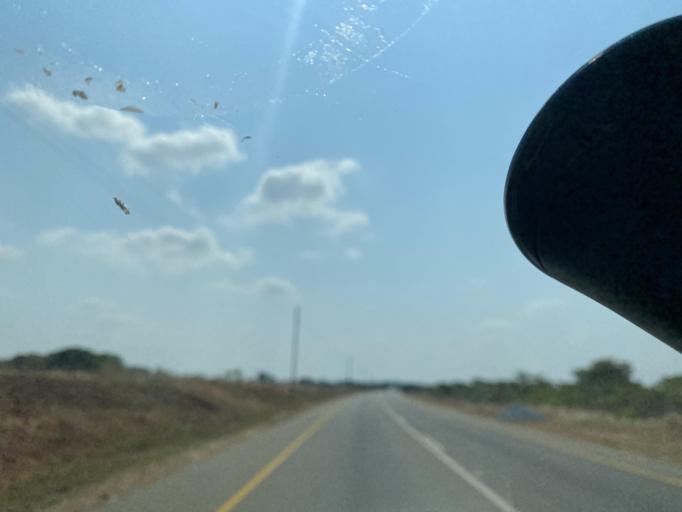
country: ZM
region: Lusaka
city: Chongwe
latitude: -15.5293
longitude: 28.6166
